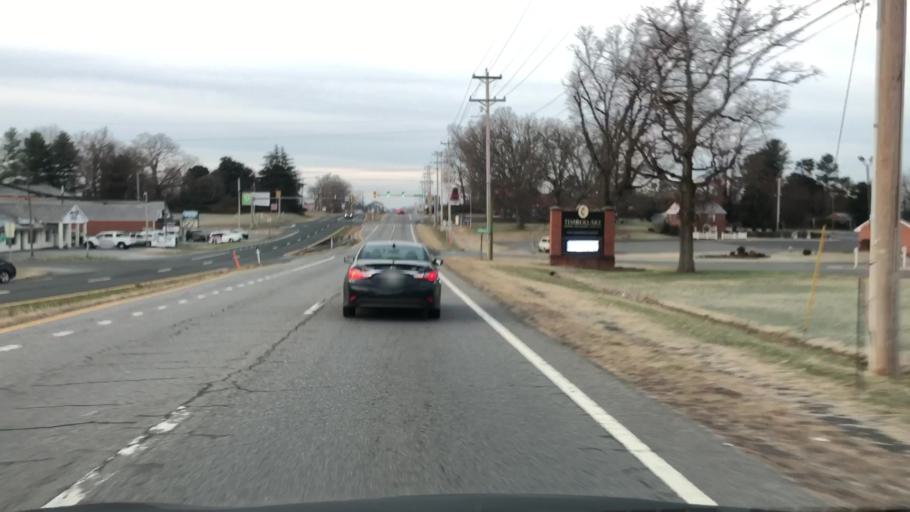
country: US
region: Virginia
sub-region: Campbell County
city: Timberlake
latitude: 37.3279
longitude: -79.2483
